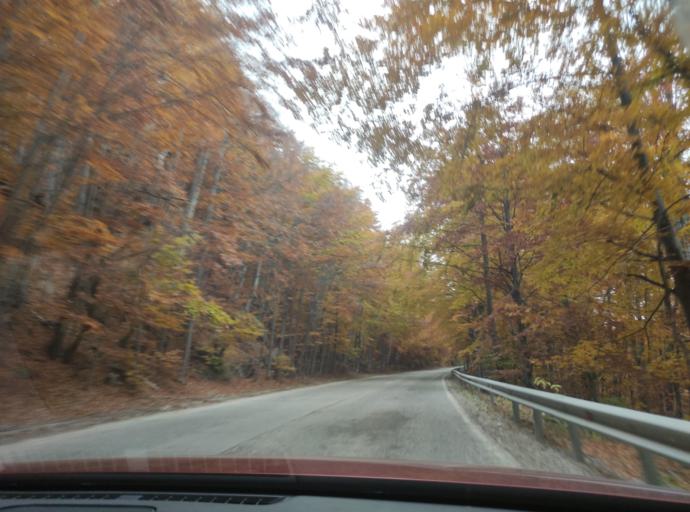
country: BG
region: Montana
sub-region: Obshtina Berkovitsa
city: Berkovitsa
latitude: 43.1158
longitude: 23.1126
